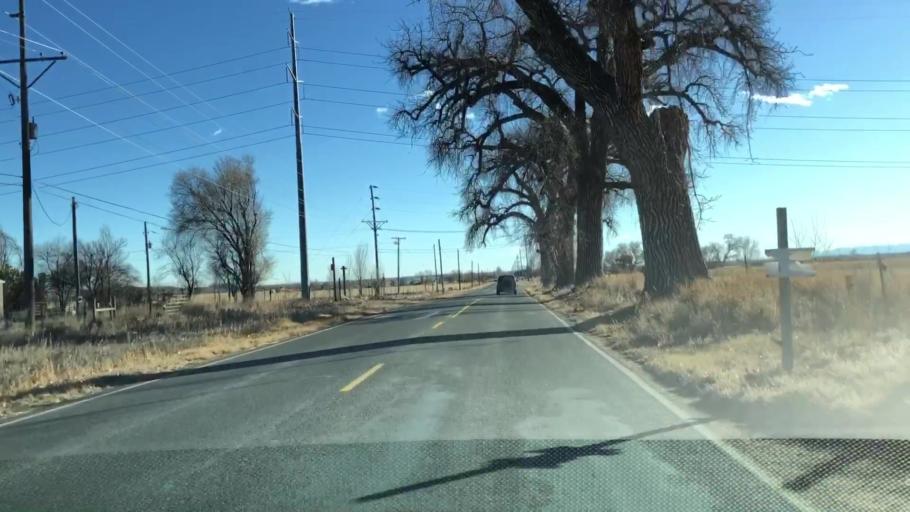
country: US
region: Colorado
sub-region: Larimer County
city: Fort Collins
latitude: 40.5604
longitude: -104.9822
